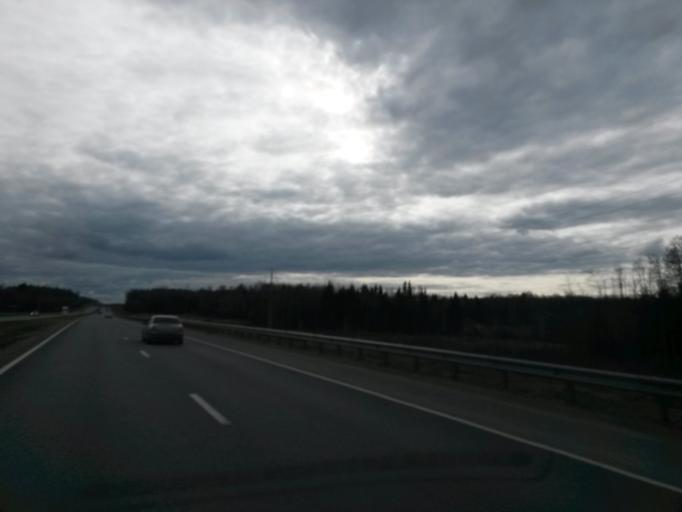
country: RU
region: Jaroslavl
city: Krasnyye Tkachi
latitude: 57.4038
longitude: 39.6534
